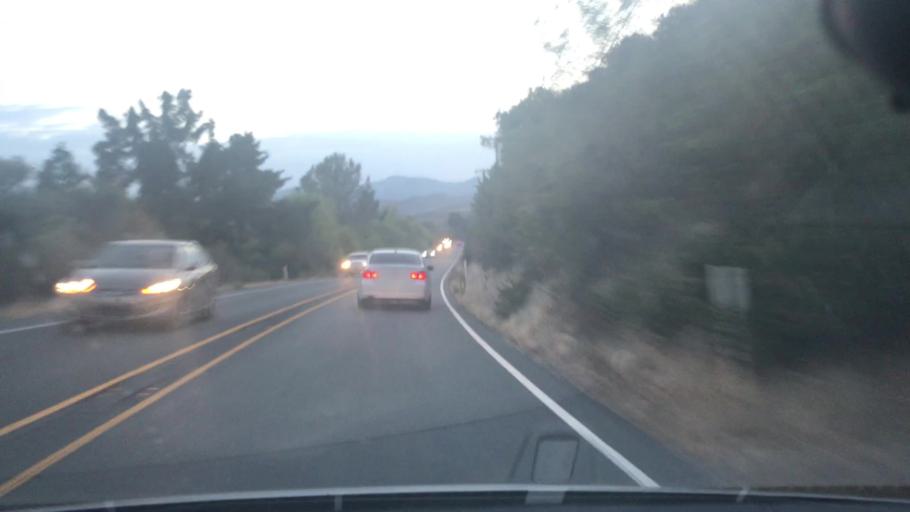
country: US
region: California
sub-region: Orange County
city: Coto De Caza
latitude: 33.5293
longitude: -117.5527
